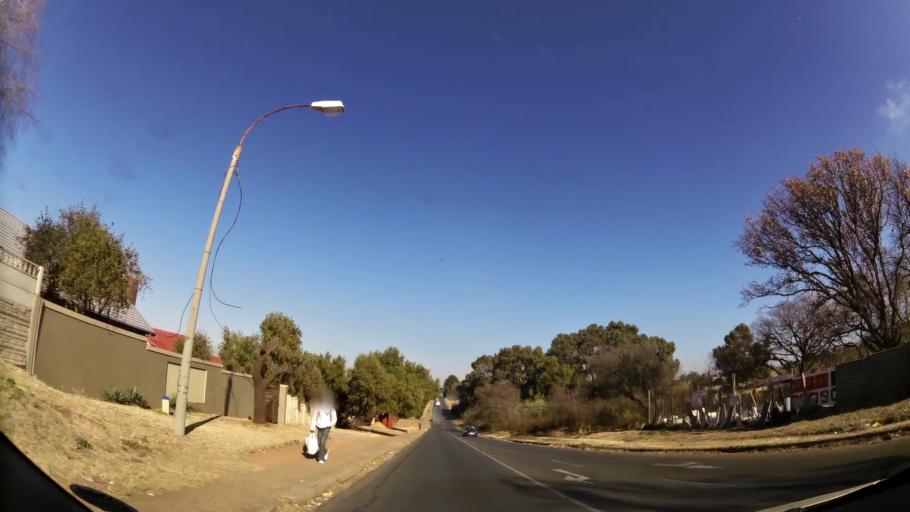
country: ZA
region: Gauteng
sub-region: City of Johannesburg Metropolitan Municipality
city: Roodepoort
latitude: -26.1504
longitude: 27.8399
